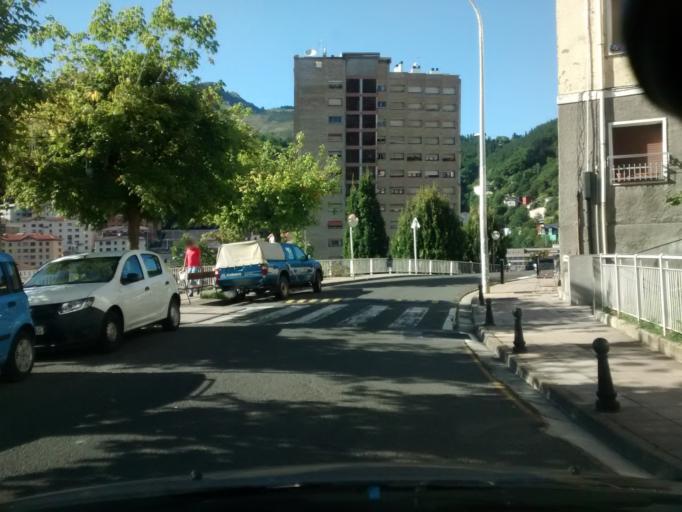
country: ES
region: Basque Country
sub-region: Provincia de Guipuzcoa
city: Eibar
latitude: 43.1830
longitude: -2.4720
